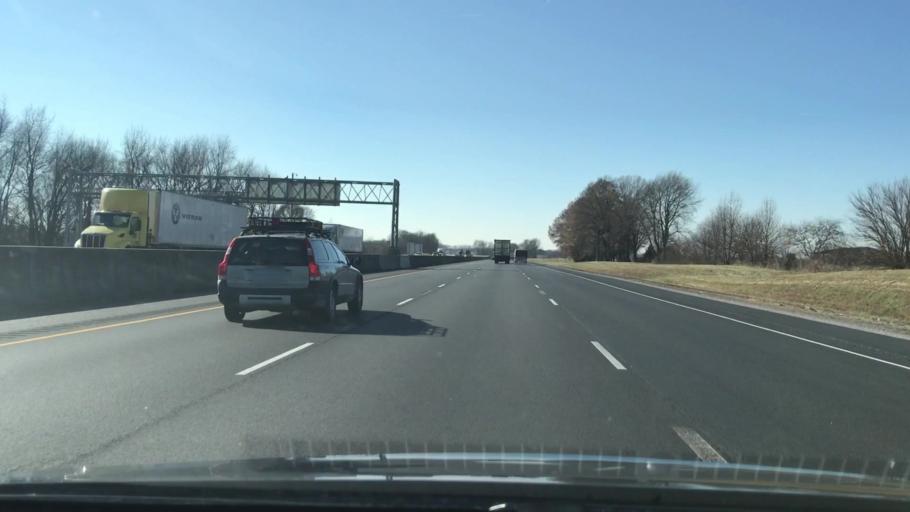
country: US
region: Kentucky
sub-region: Edmonson County
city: Brownsville
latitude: 37.0385
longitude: -86.2264
